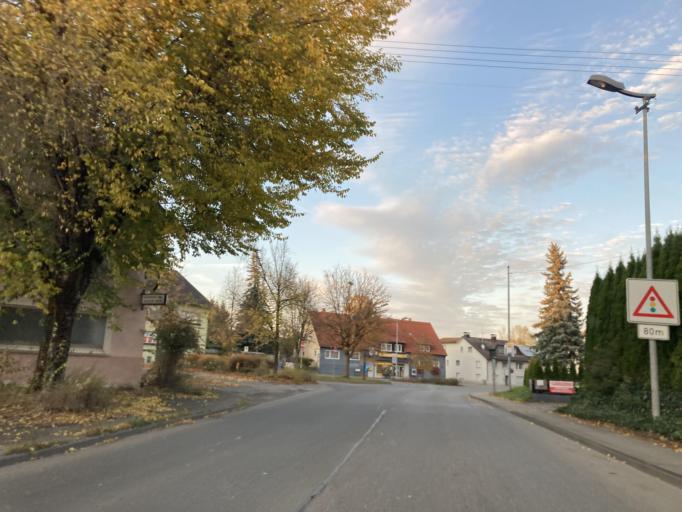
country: DE
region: Baden-Wuerttemberg
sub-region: Tuebingen Region
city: Zimmern unter der Burg
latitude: 48.1960
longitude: 8.6976
